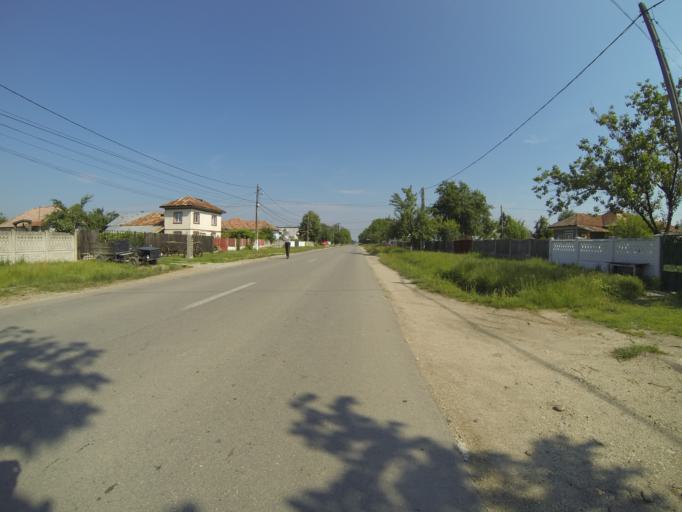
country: RO
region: Gorj
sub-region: Comuna Crusetu
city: Crusetu
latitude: 44.6047
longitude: 23.6899
